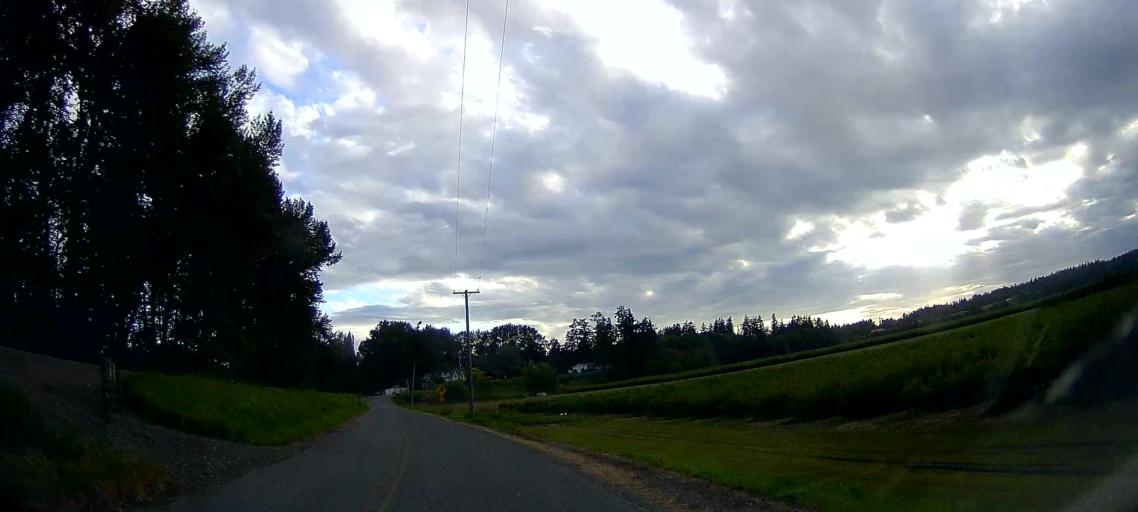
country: US
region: Washington
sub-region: Skagit County
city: Mount Vernon
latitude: 48.3669
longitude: -122.4142
